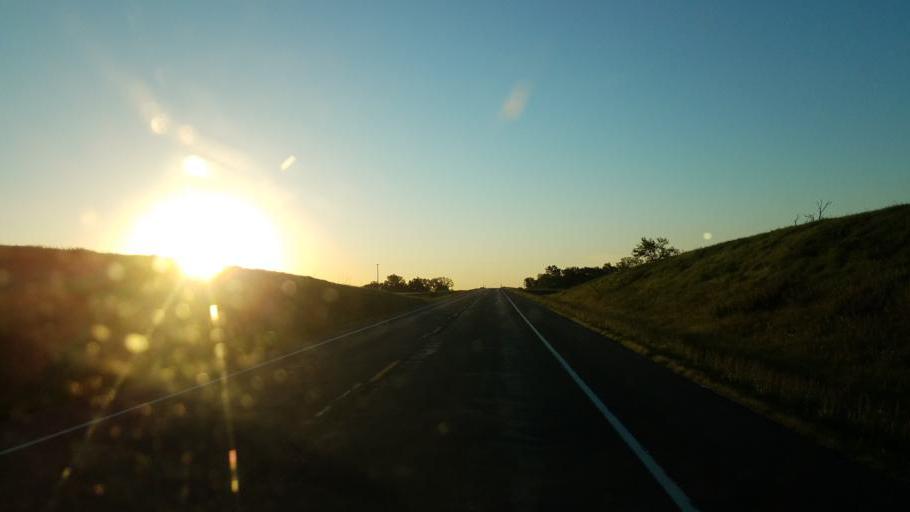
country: US
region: Missouri
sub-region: Schuyler County
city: Lancaster
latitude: 40.4927
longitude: -92.5831
